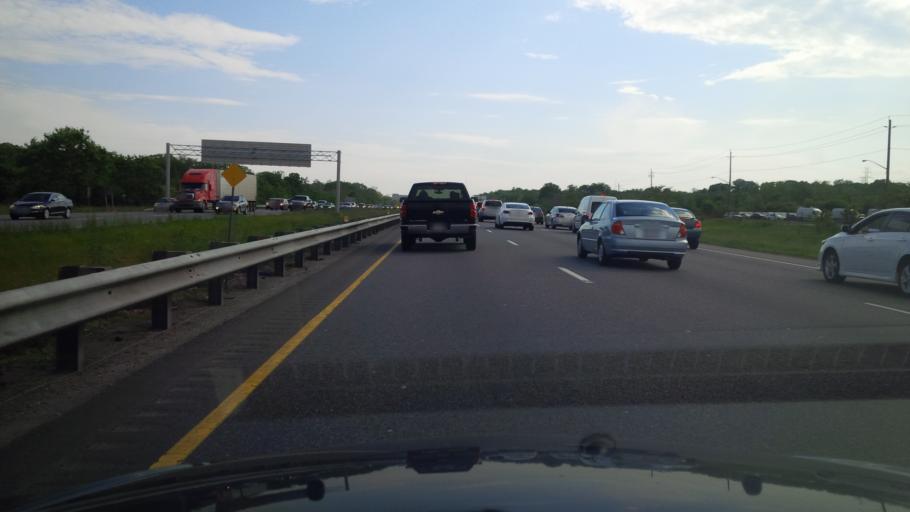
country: CA
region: Ontario
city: Burlington
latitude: 43.3238
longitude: -79.8479
